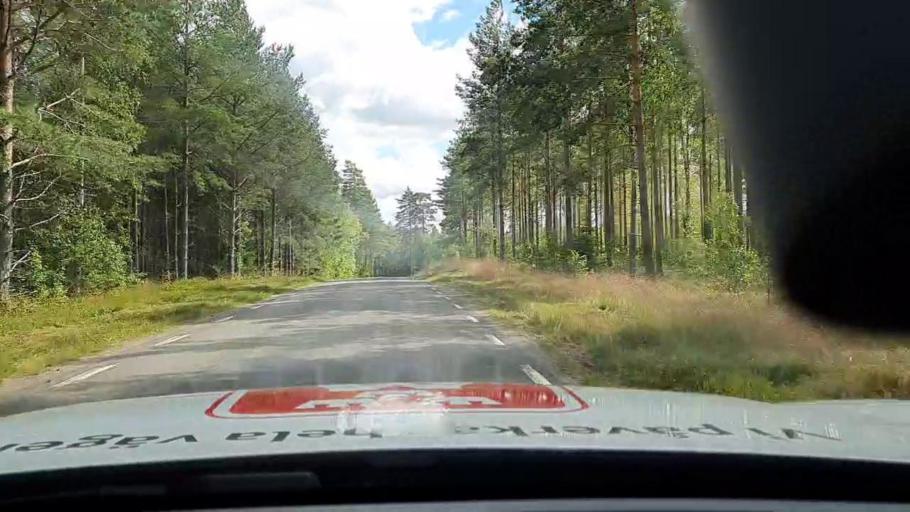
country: SE
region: Vaestra Goetaland
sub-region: Karlsborgs Kommun
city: Molltorp
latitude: 58.6059
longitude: 14.3670
